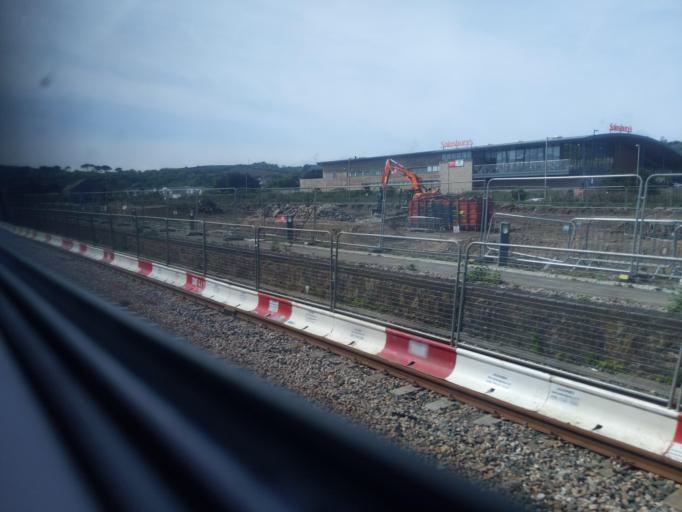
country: GB
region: England
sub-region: Cornwall
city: Penzance
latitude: 50.1272
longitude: -5.5171
